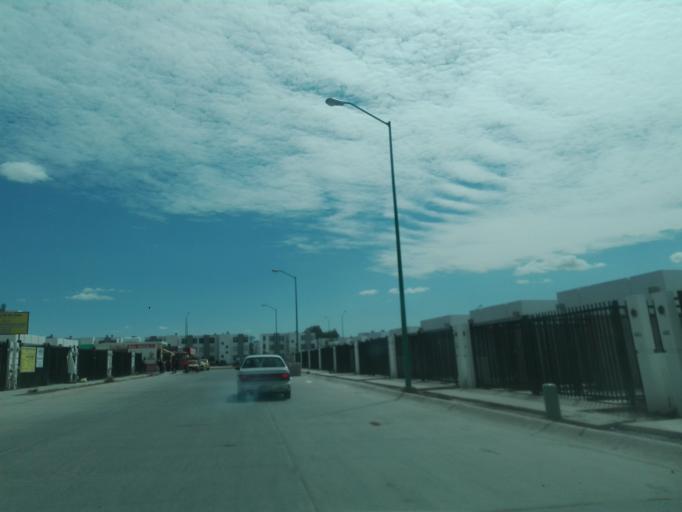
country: MX
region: Guanajuato
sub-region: Leon
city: Ladrilleras del Refugio
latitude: 21.0690
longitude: -101.5596
